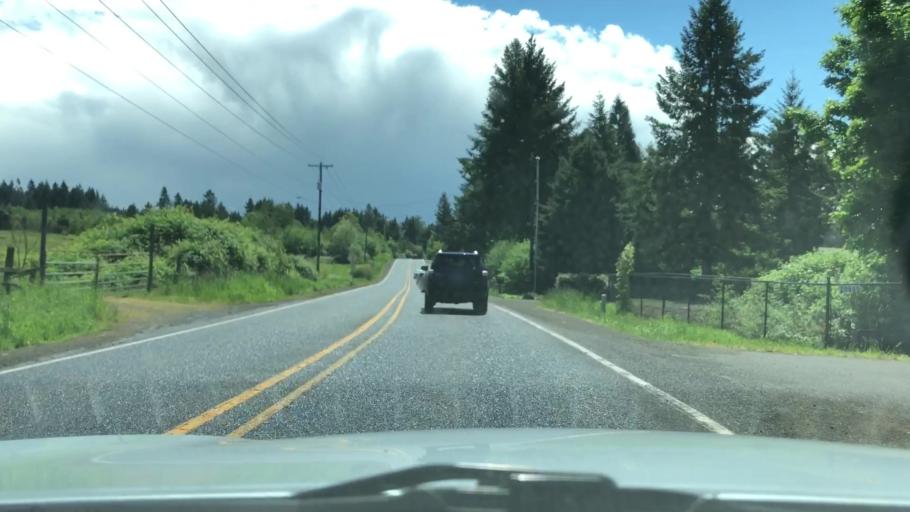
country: US
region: Oregon
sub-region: Clackamas County
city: Beavercreek
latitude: 45.3049
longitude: -122.5444
